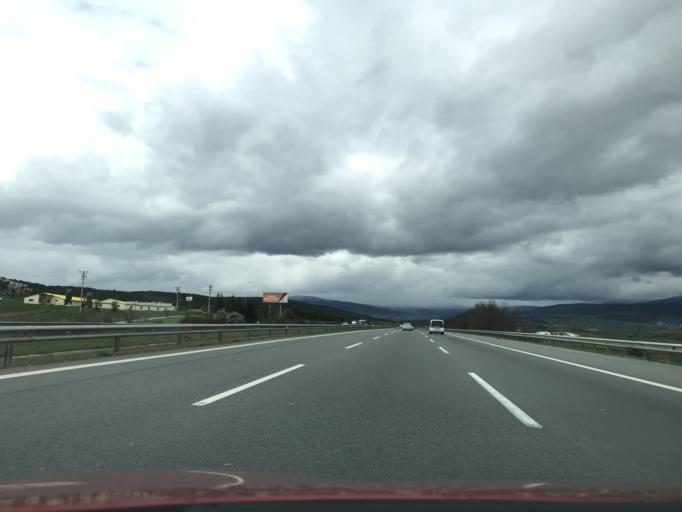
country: TR
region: Bolu
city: Bolu
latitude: 40.7771
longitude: 31.6948
